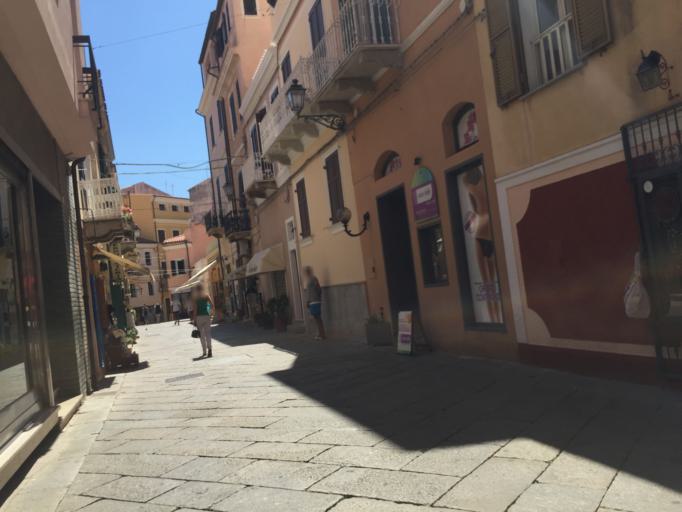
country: IT
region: Sardinia
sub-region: Provincia di Olbia-Tempio
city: La Maddalena
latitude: 41.2136
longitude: 9.4073
